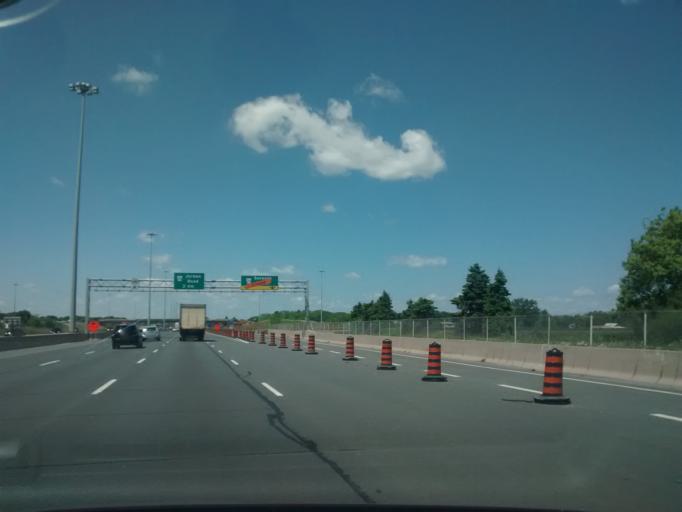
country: CA
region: Ontario
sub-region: Regional Municipality of Niagara
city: St. Catharines
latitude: 43.1791
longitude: -79.3027
